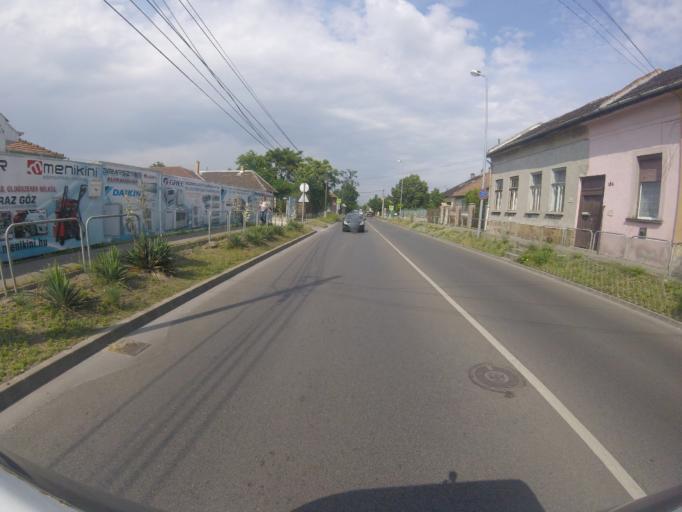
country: HU
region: Budapest
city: Budapest XIX. keruelet
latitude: 47.4473
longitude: 19.1283
